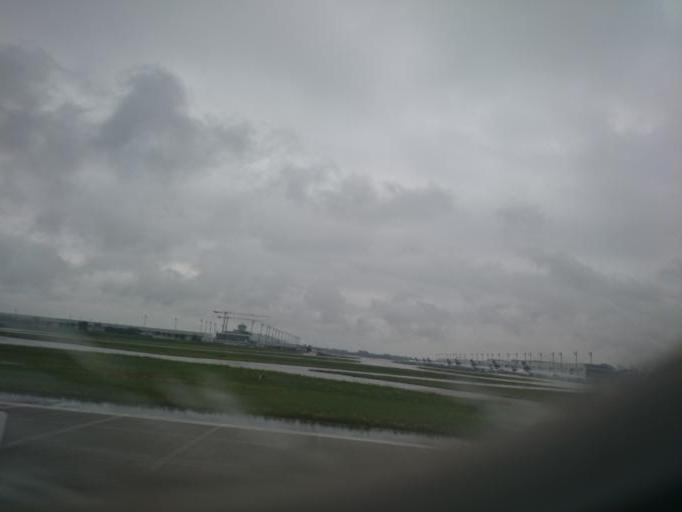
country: DE
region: Bavaria
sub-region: Upper Bavaria
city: Marzling
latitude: 48.3649
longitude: 11.7941
